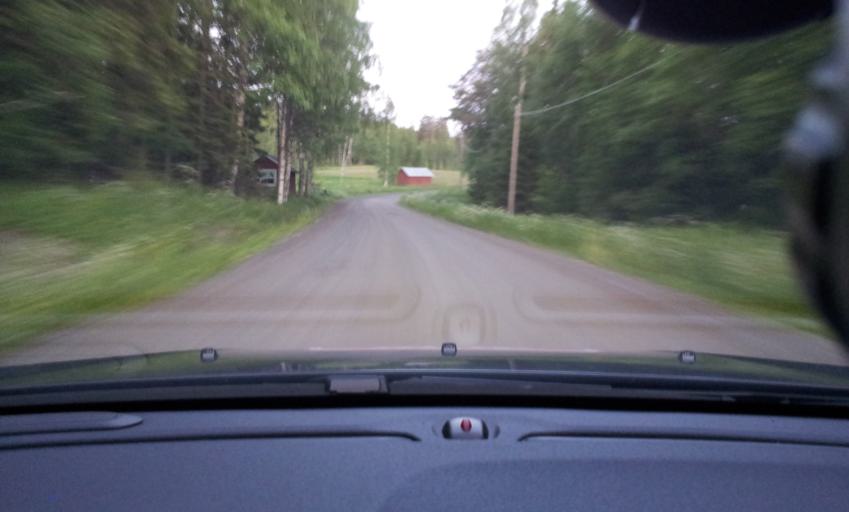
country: SE
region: Jaemtland
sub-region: Ragunda Kommun
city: Hammarstrand
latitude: 62.9063
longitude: 16.0932
